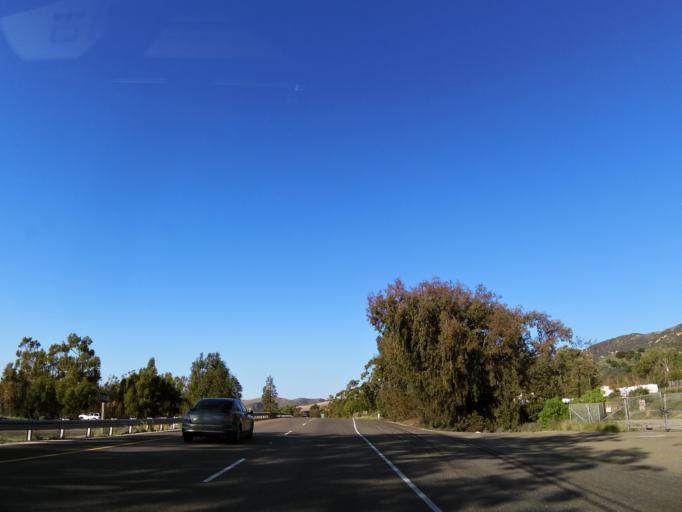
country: US
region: California
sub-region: Santa Barbara County
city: Solvang
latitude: 34.4733
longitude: -120.1978
